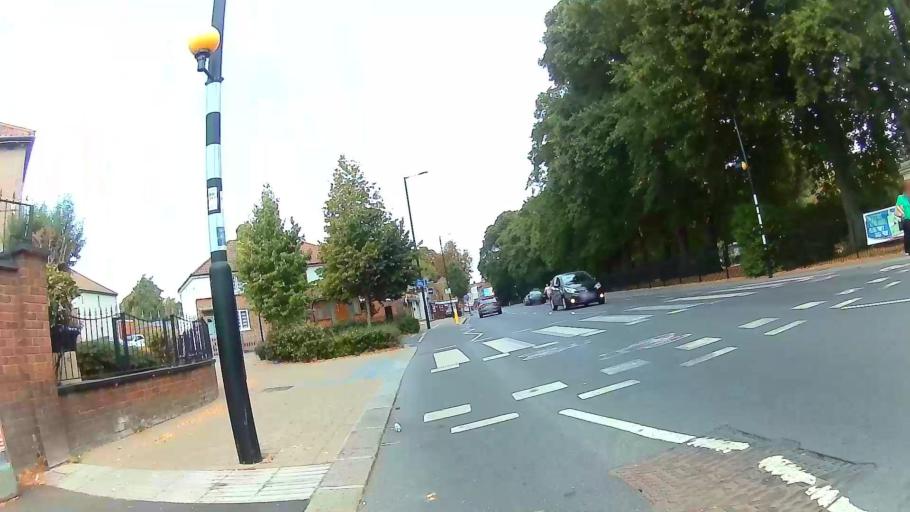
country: GB
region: England
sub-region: Greater London
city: Enfield
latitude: 51.6548
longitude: -0.0483
